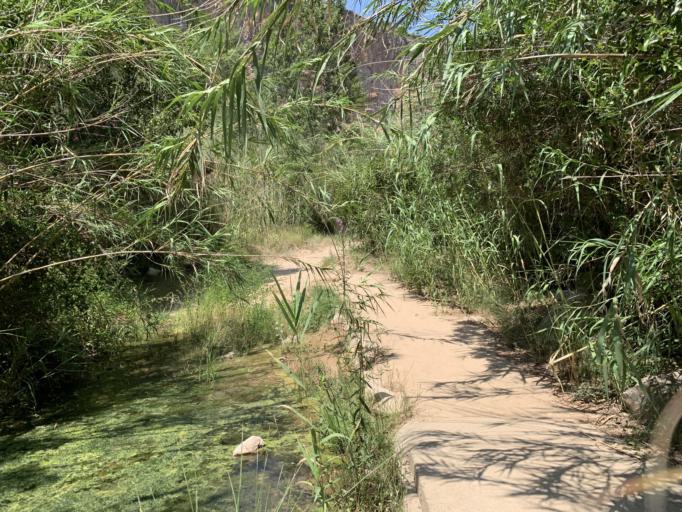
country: ES
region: Valencia
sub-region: Provincia de Valencia
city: Chulilla
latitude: 39.6603
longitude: -0.8931
